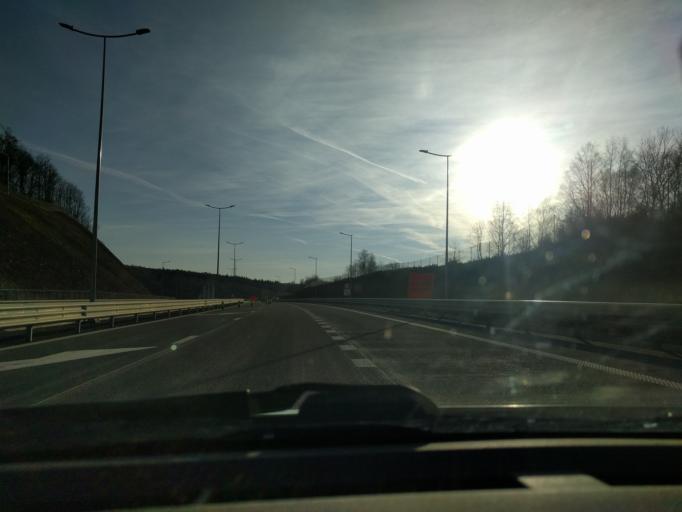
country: BE
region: Wallonia
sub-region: Province de Namur
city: Couvin
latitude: 50.0414
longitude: 4.5091
